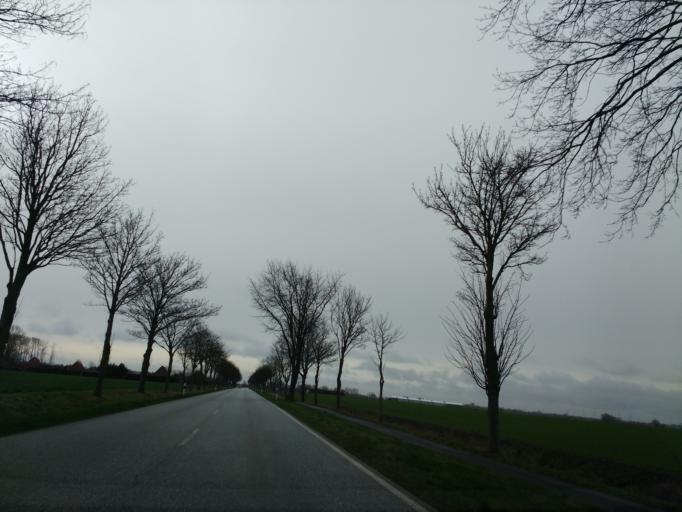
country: DE
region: Schleswig-Holstein
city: Grube
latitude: 54.2503
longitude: 11.0313
